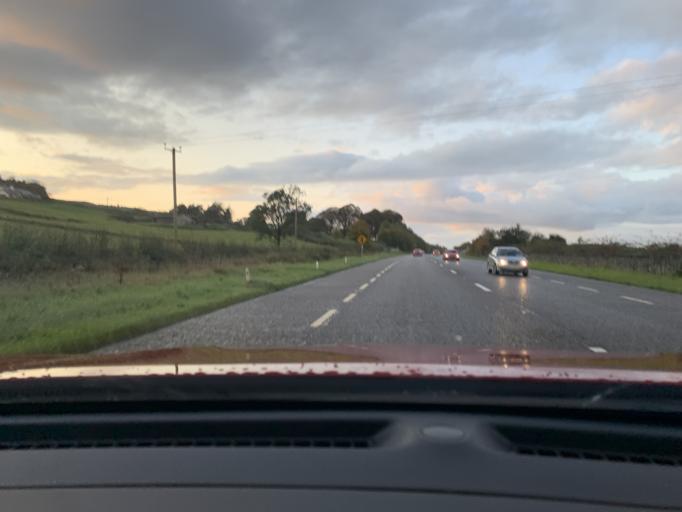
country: IE
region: Connaught
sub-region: Roscommon
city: Boyle
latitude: 54.0639
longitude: -8.3560
